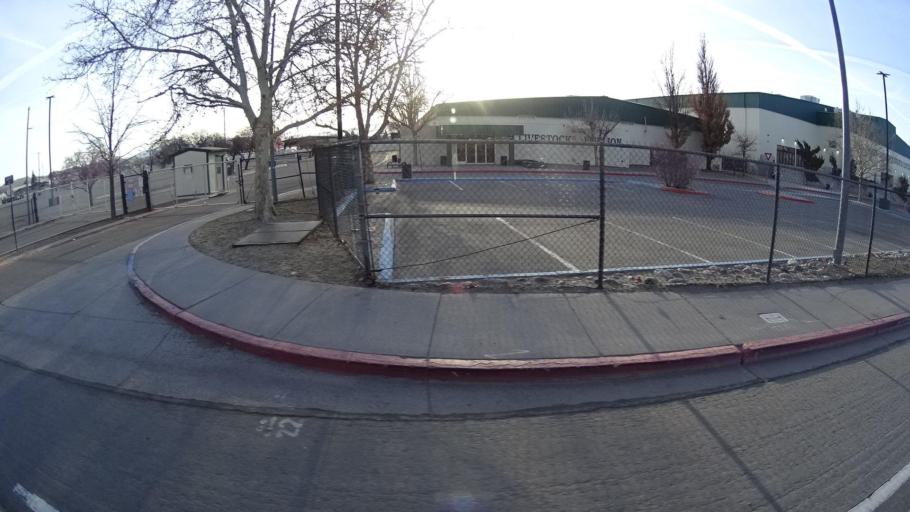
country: US
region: Nevada
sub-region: Washoe County
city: Reno
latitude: 39.5433
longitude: -119.8029
